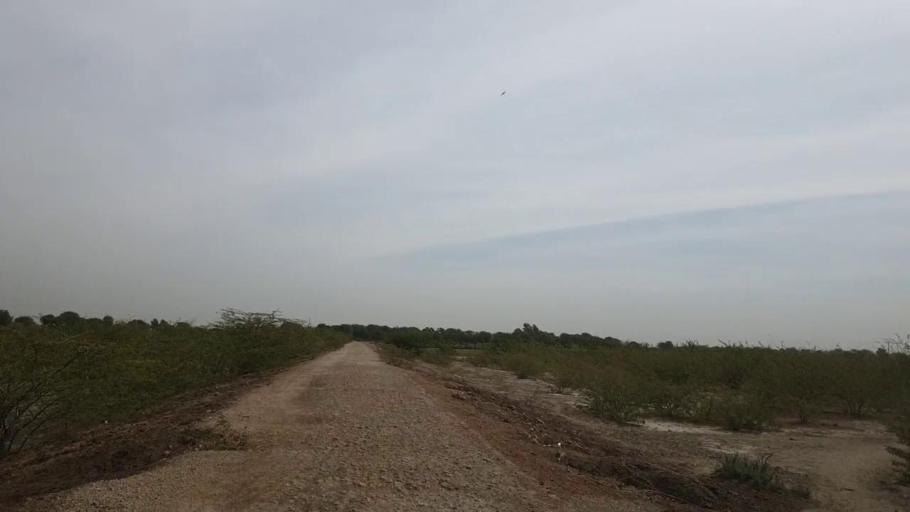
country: PK
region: Sindh
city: Kunri
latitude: 25.1844
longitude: 69.5988
